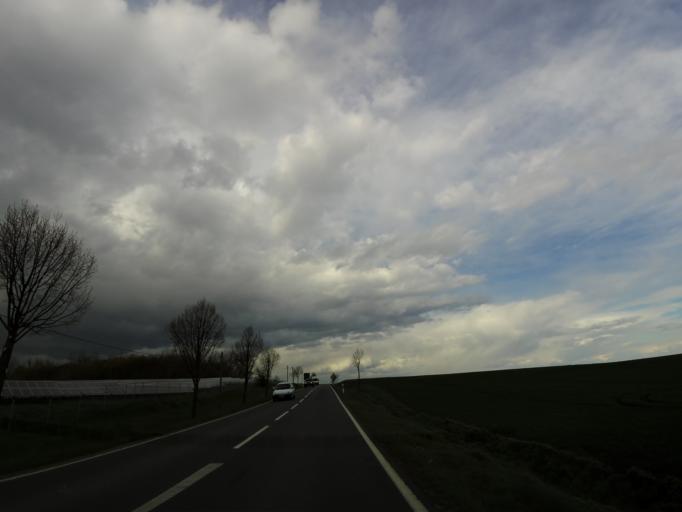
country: DE
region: Saxony-Anhalt
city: Ditfurt
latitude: 51.8194
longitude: 11.2140
